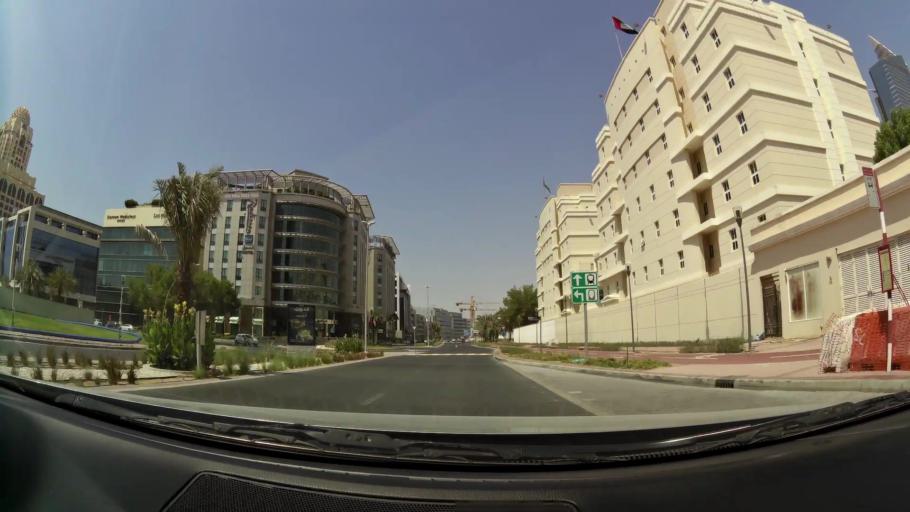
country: AE
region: Dubai
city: Dubai
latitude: 25.0928
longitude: 55.1549
